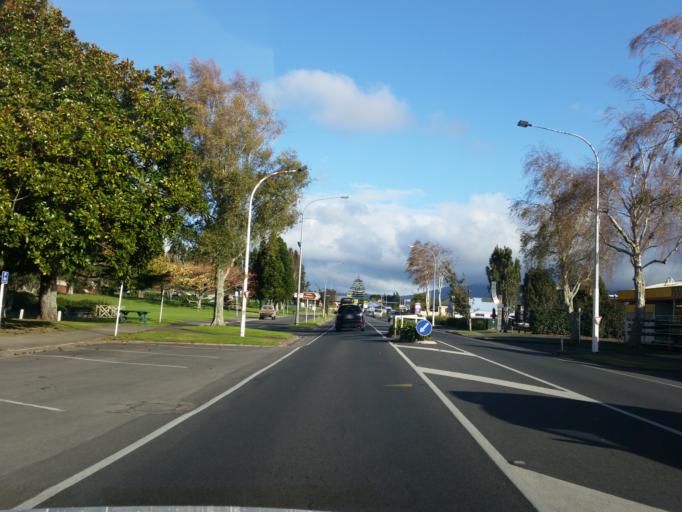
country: NZ
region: Bay of Plenty
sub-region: Western Bay of Plenty District
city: Katikati
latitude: -37.5549
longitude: 175.9170
